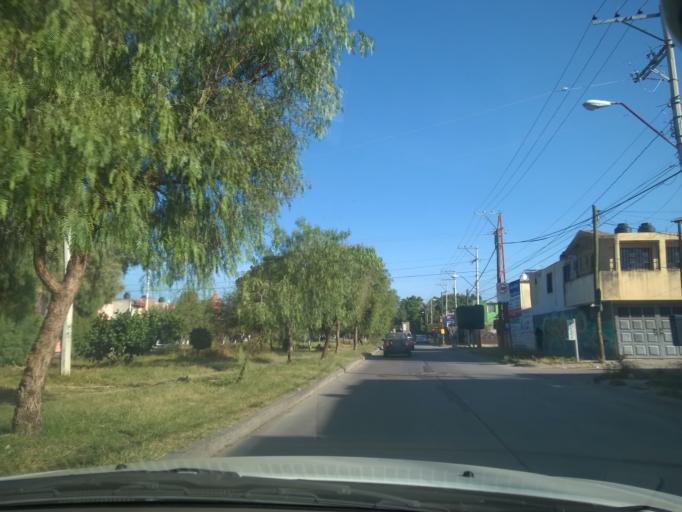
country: MX
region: Guanajuato
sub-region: Leon
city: San Jose de Duran (Los Troncoso)
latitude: 21.0739
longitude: -101.6452
